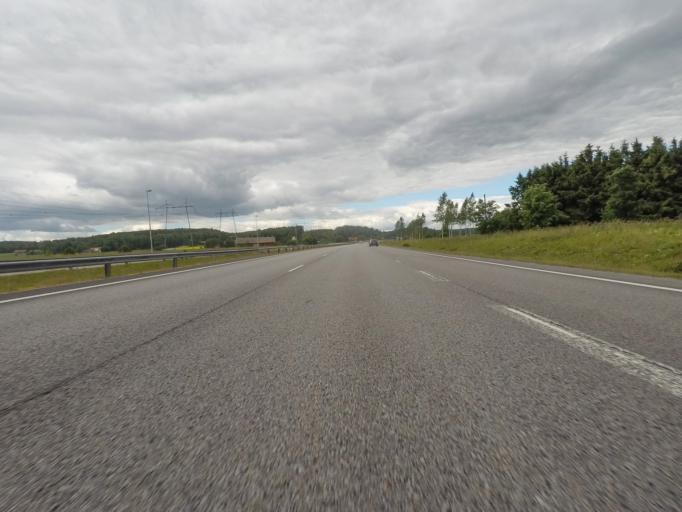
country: FI
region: Varsinais-Suomi
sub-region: Turku
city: Paimio
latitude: 60.4269
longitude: 22.6646
